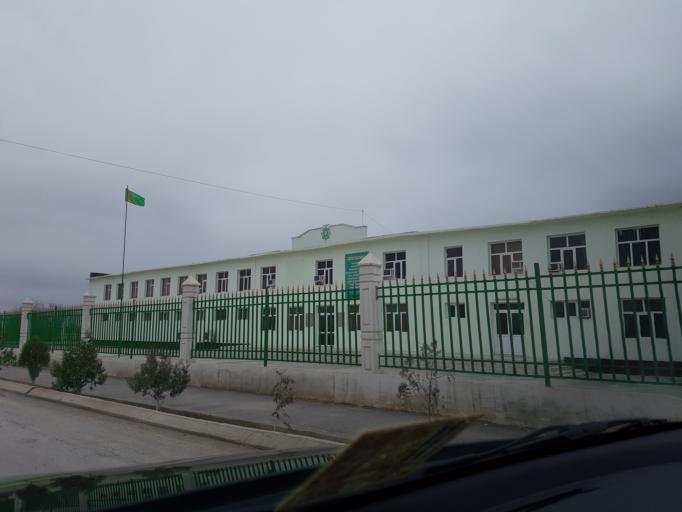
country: TM
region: Ahal
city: Abadan
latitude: 38.1440
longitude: 57.9526
